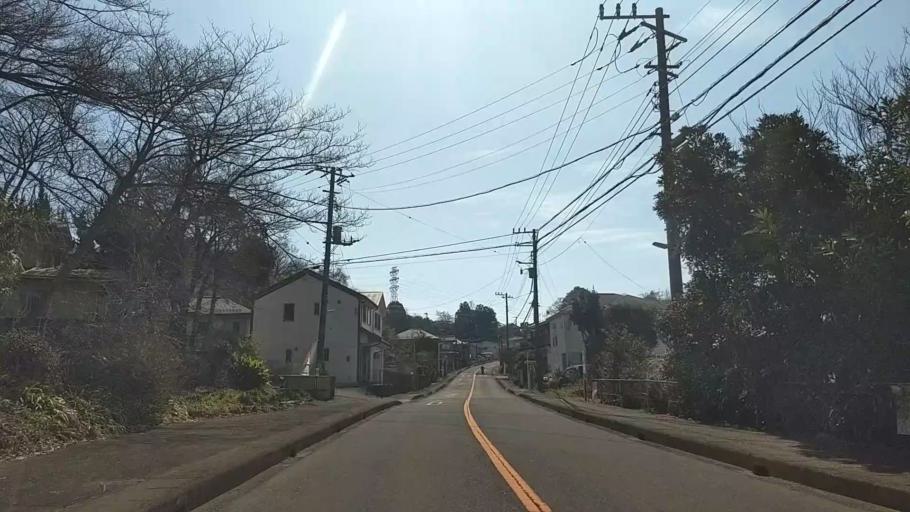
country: JP
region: Kanagawa
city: Chigasaki
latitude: 35.3735
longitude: 139.4273
